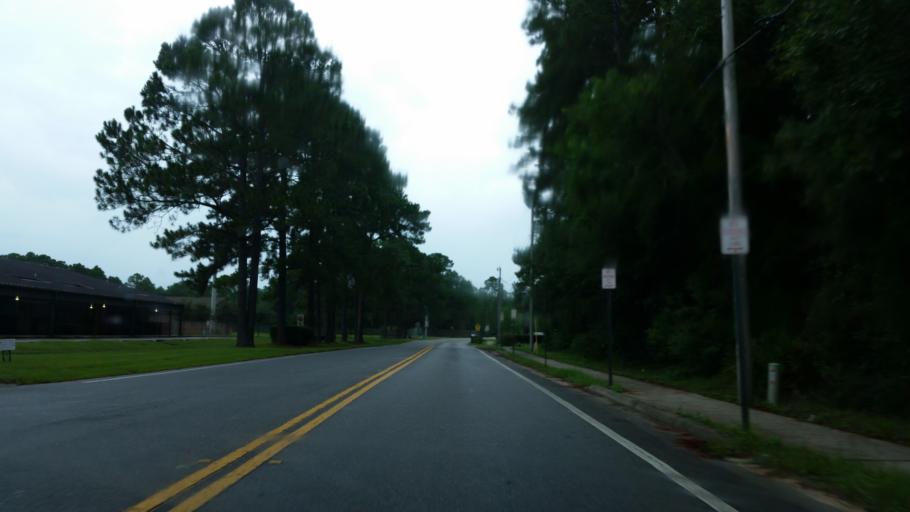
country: US
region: Florida
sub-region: Escambia County
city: Warrington
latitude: 30.3884
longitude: -87.2895
